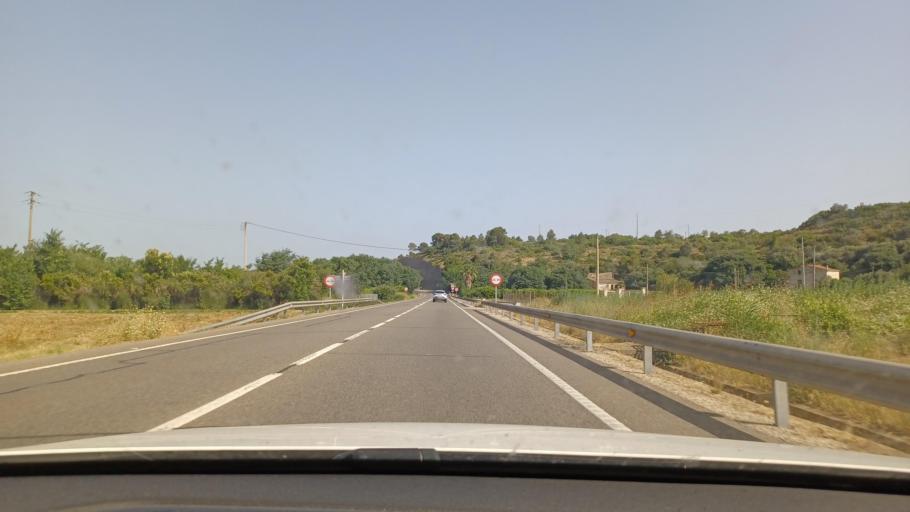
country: ES
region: Catalonia
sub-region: Provincia de Tarragona
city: Tortosa
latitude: 40.7781
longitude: 0.5073
